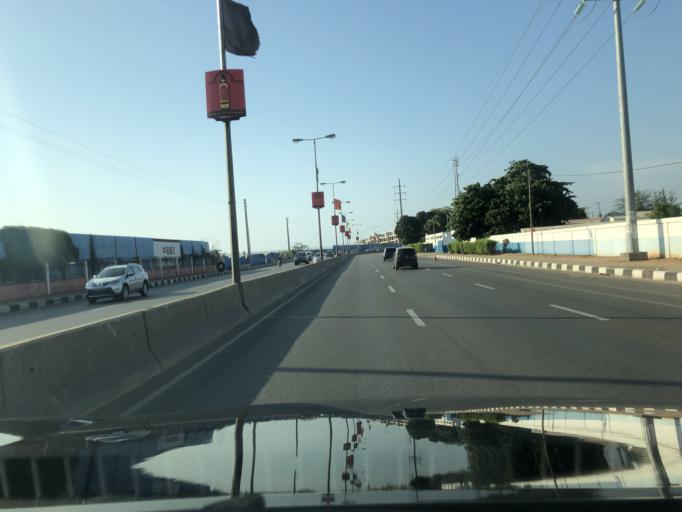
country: AO
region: Luanda
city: Luanda
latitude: -8.9011
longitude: 13.1768
